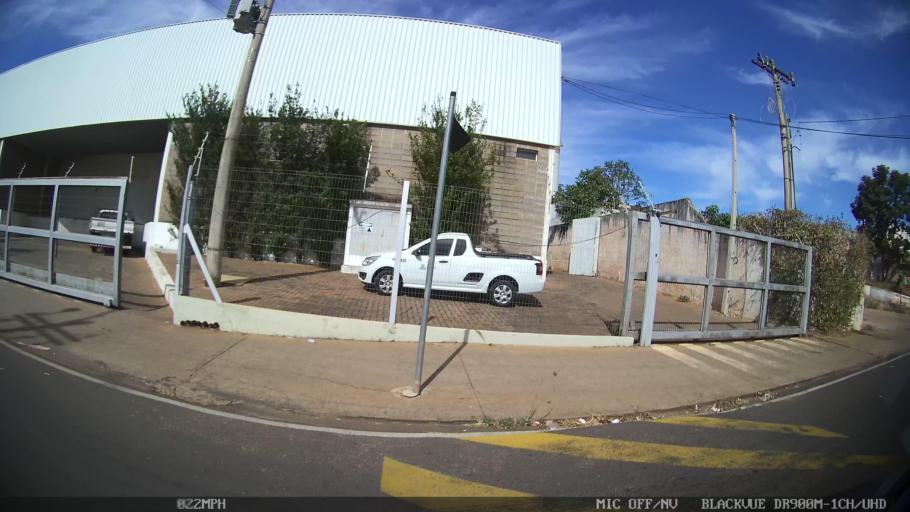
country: BR
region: Sao Paulo
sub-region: Sao Jose Do Rio Preto
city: Sao Jose do Rio Preto
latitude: -20.8451
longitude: -49.3470
